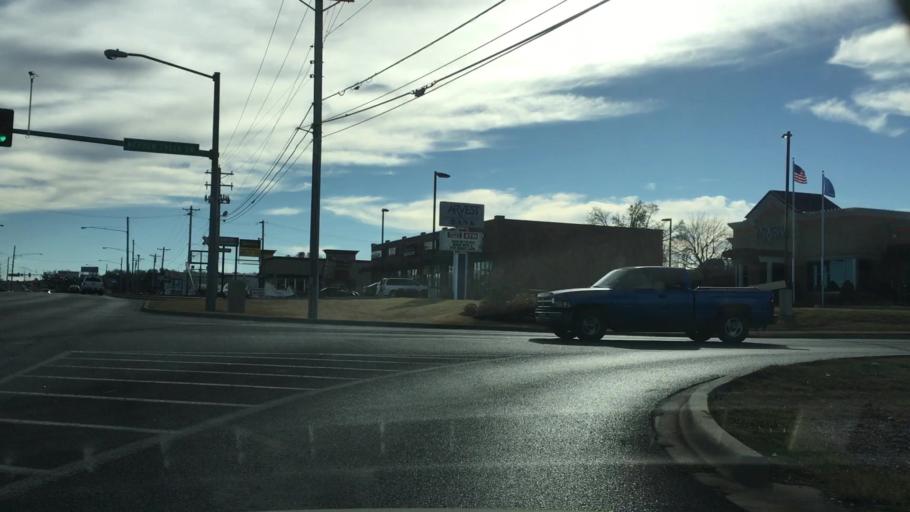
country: US
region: Oklahoma
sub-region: Cherokee County
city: Tahlequah
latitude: 35.8932
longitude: -94.9773
